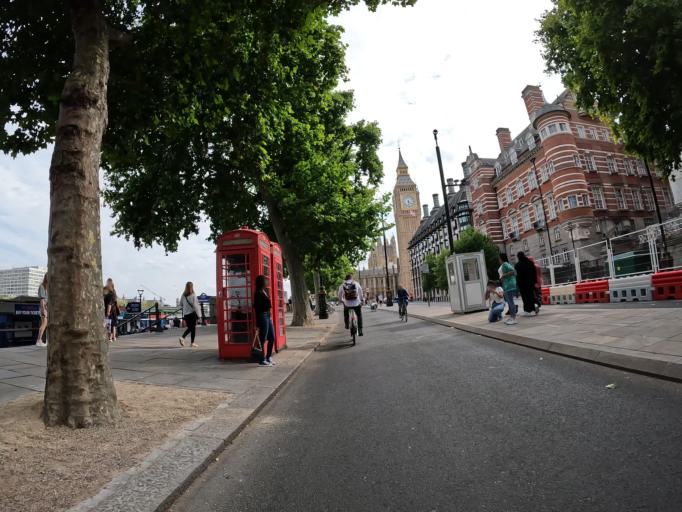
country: GB
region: England
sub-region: Greater London
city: Orpington
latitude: 51.3680
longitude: 0.0501
